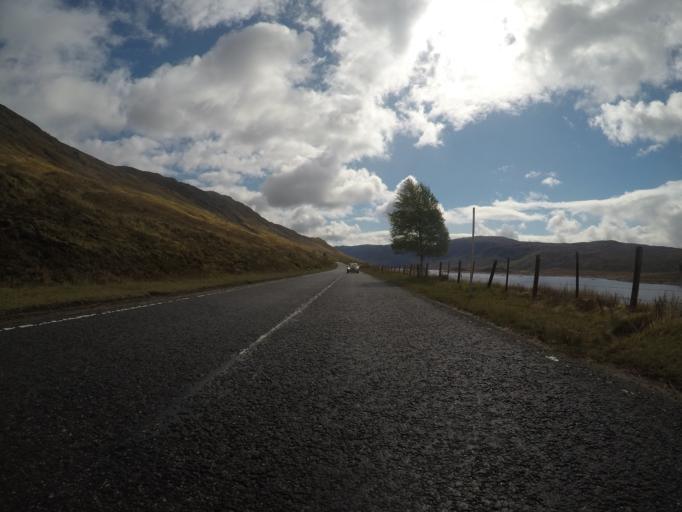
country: GB
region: Scotland
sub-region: Highland
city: Fort William
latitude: 57.1564
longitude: -5.1464
